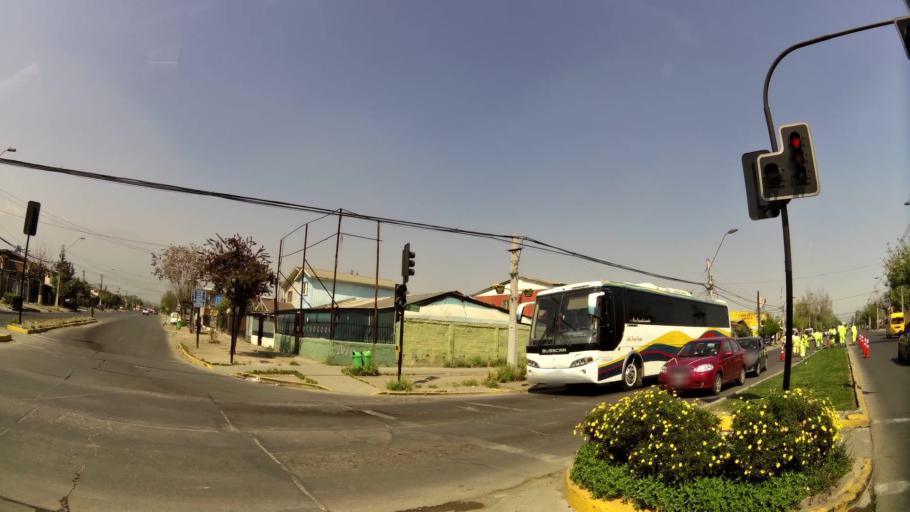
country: CL
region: Santiago Metropolitan
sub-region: Provincia de Santiago
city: La Pintana
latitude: -33.5430
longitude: -70.6036
